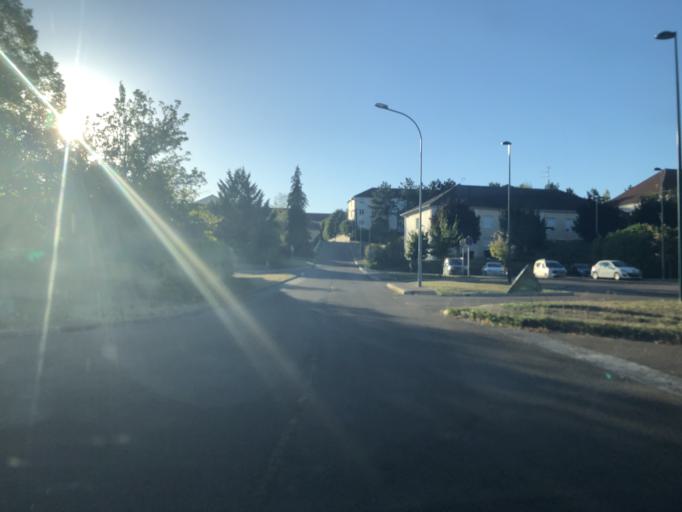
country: FR
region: Bourgogne
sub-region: Departement de l'Yonne
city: Joigny
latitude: 47.9828
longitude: 3.4098
